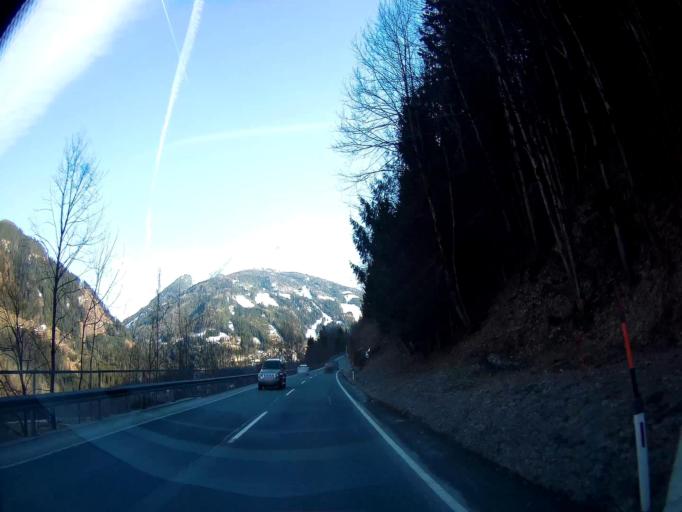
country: AT
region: Salzburg
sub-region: Politischer Bezirk Sankt Johann im Pongau
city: Bad Gastein
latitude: 47.1373
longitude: 13.1252
